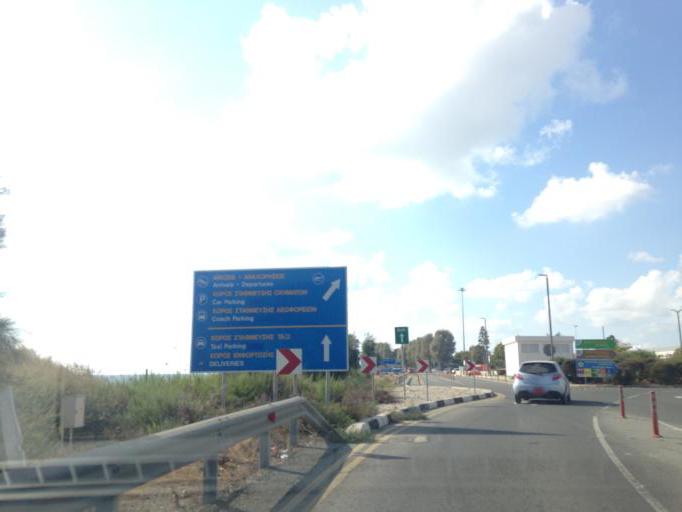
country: CY
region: Pafos
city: Paphos
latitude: 34.7102
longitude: 32.4882
